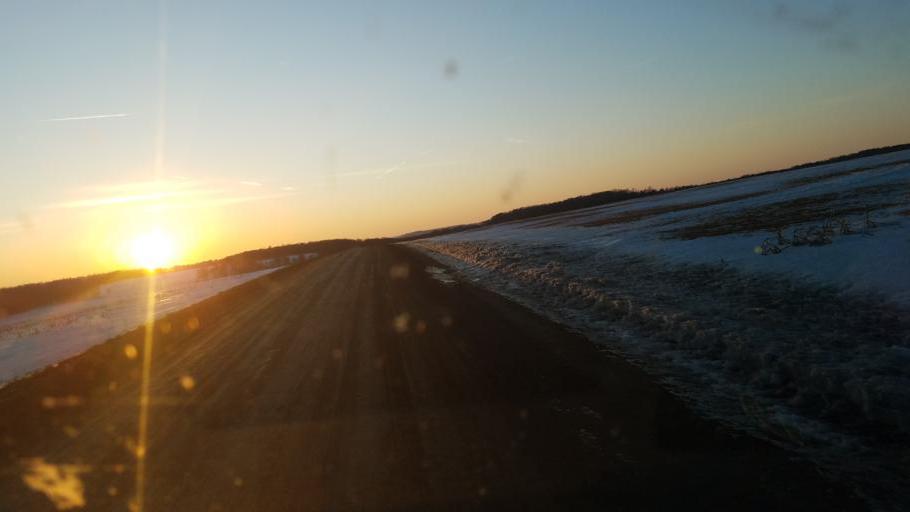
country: US
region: Pennsylvania
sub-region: Tioga County
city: Westfield
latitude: 42.0128
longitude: -77.6708
